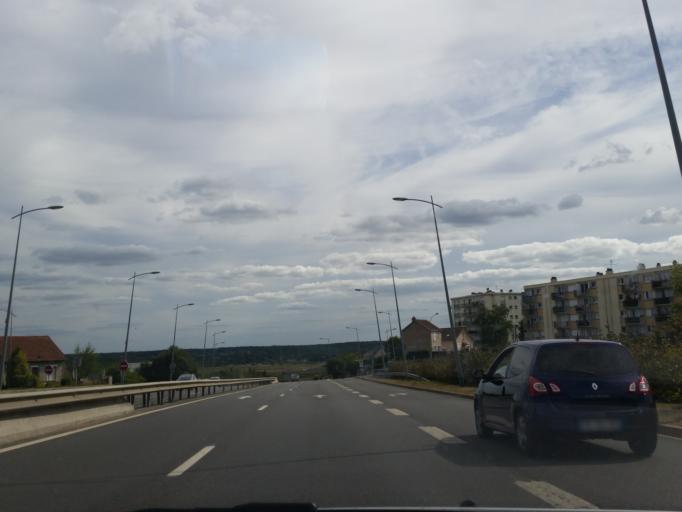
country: FR
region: Centre
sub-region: Departement du Loir-et-Cher
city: Blois
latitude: 47.6000
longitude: 1.3496
